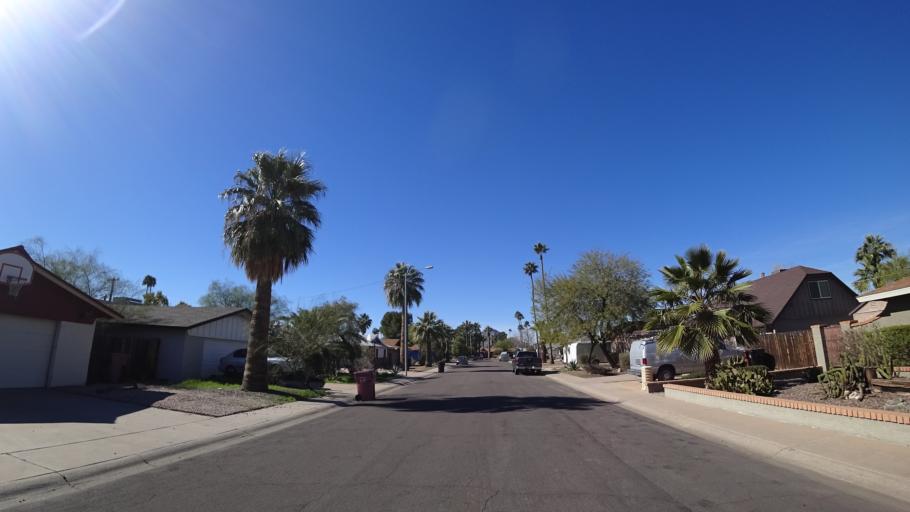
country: US
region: Arizona
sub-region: Maricopa County
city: Scottsdale
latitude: 33.5145
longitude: -111.8961
